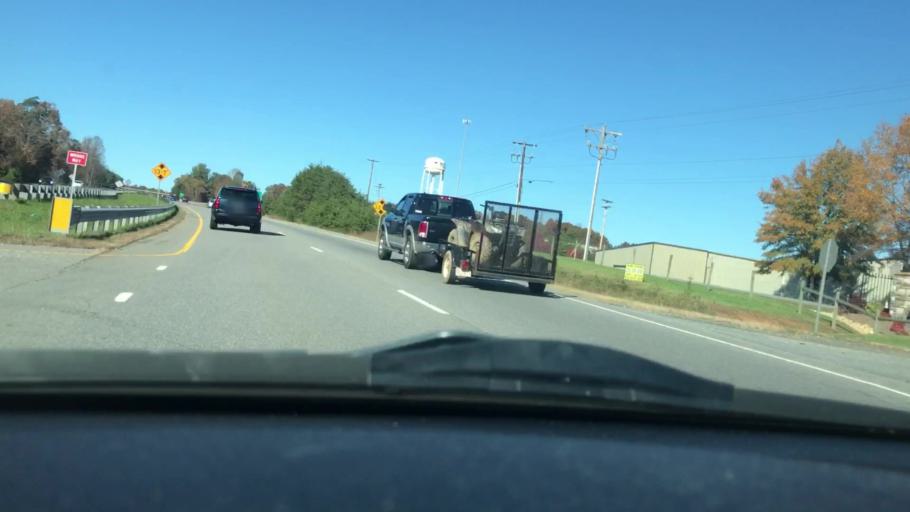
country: US
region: North Carolina
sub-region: Rockingham County
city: Stoneville
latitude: 36.4602
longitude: -79.9261
